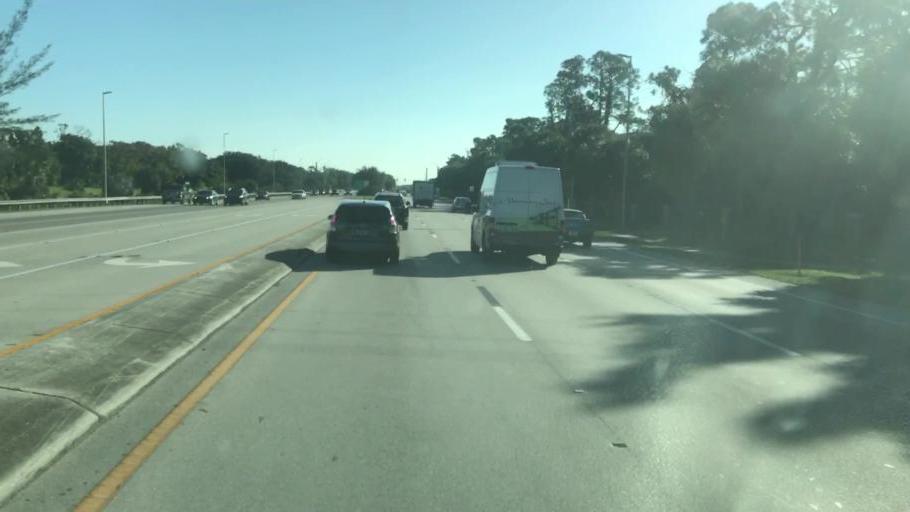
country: US
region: Florida
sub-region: Lee County
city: Villas
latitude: 26.5463
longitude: -81.8675
